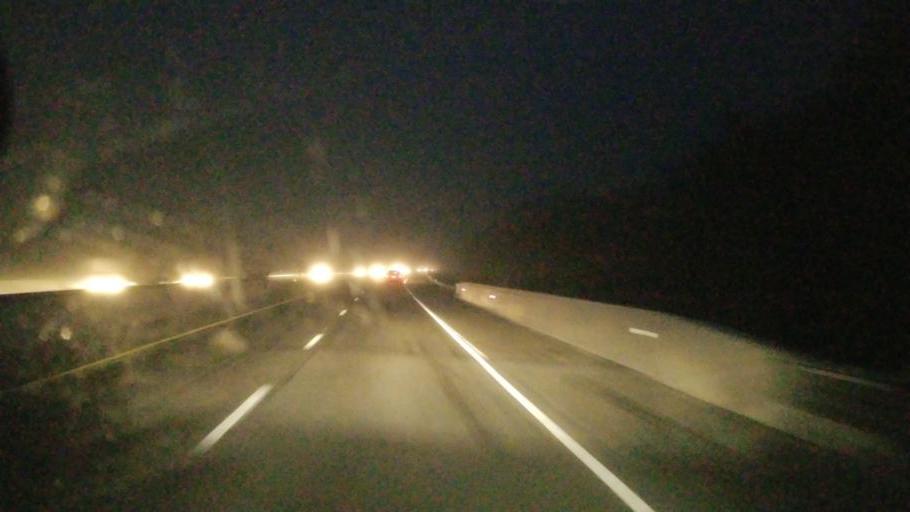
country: US
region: Ohio
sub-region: Ross County
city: Kingston
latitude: 39.4631
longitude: -82.9700
